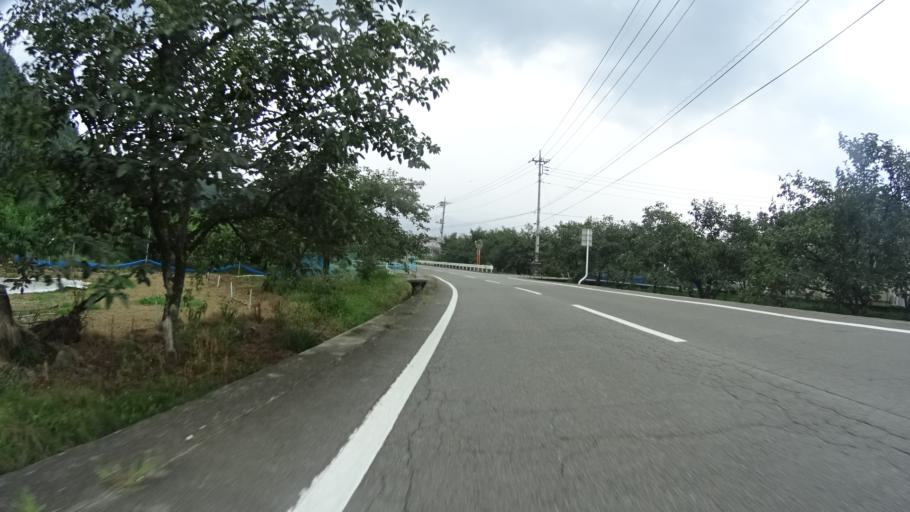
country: JP
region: Yamanashi
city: Enzan
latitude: 35.7298
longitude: 138.7228
